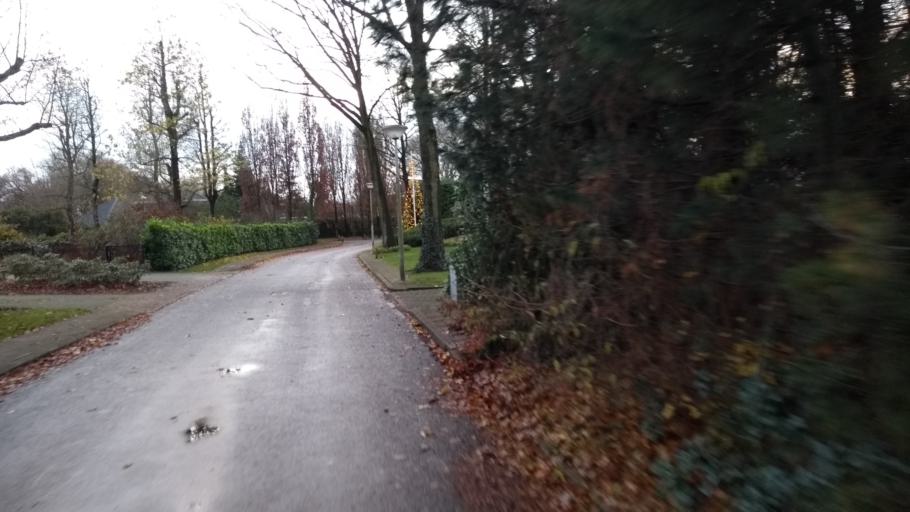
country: NL
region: Overijssel
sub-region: Gemeente Almelo
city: Almelo
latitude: 52.3541
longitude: 6.6838
